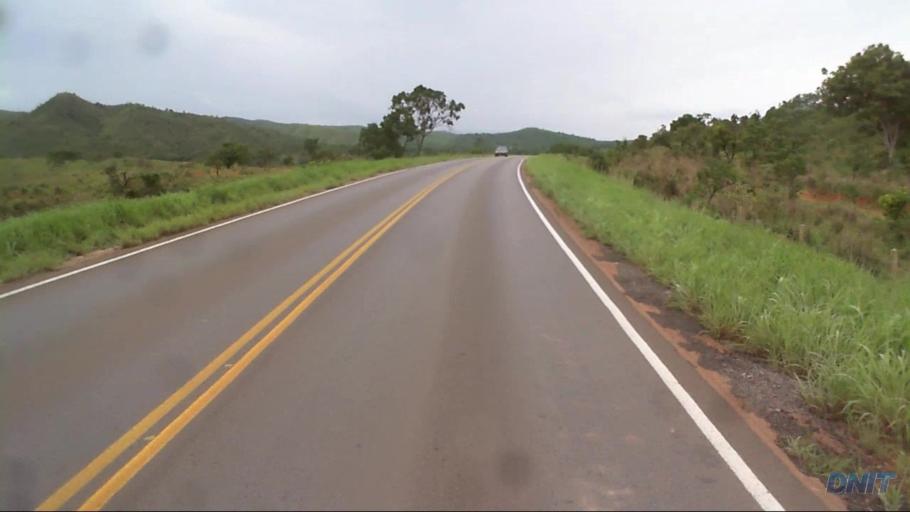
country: BR
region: Goias
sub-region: Padre Bernardo
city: Padre Bernardo
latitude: -15.4385
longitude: -48.1939
